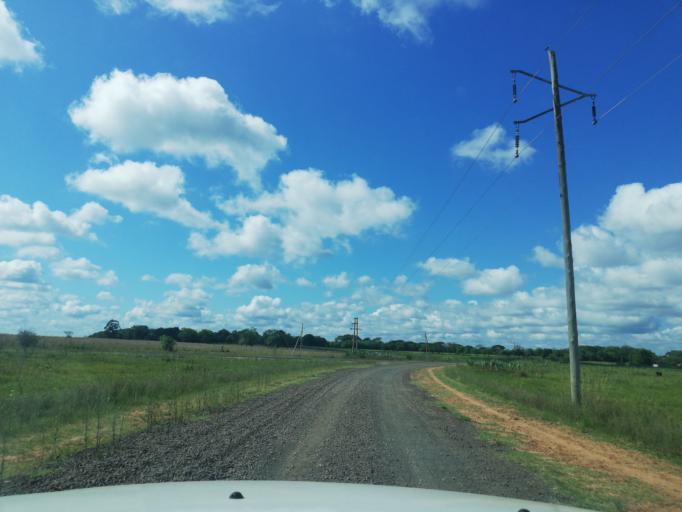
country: AR
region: Corrientes
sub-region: Departamento de San Miguel
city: San Miguel
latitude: -27.9809
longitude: -57.5807
